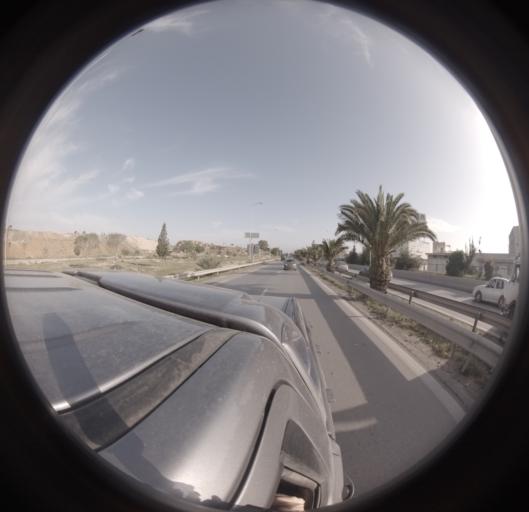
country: TN
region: Bin 'Arus
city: Ben Arous
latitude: 36.7712
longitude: 10.1982
